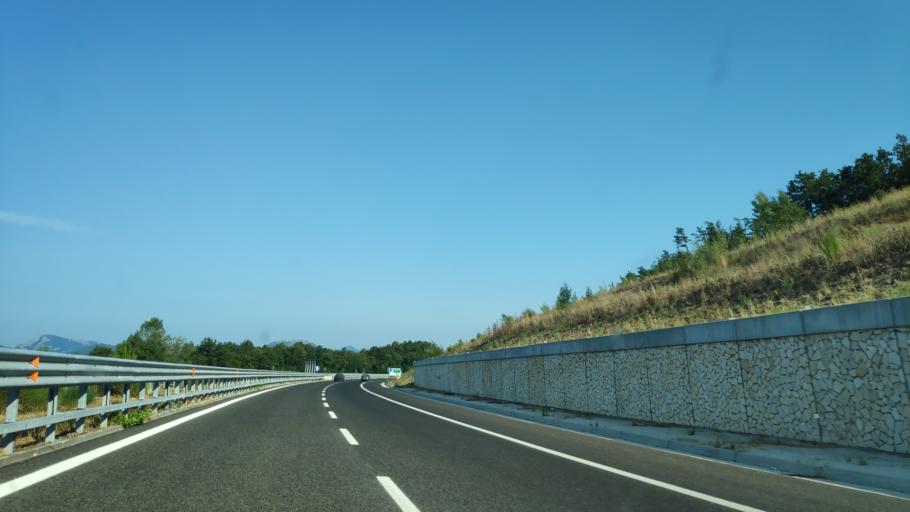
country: IT
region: Basilicate
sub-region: Provincia di Potenza
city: Nemoli
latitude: 40.1023
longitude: 15.7986
